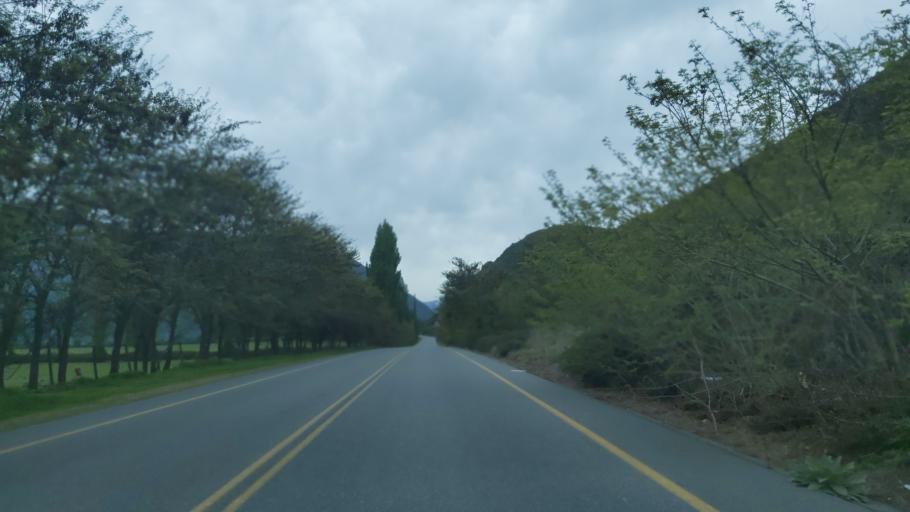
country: CL
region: Maule
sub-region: Provincia de Linares
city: Colbun
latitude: -35.8128
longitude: -70.8616
